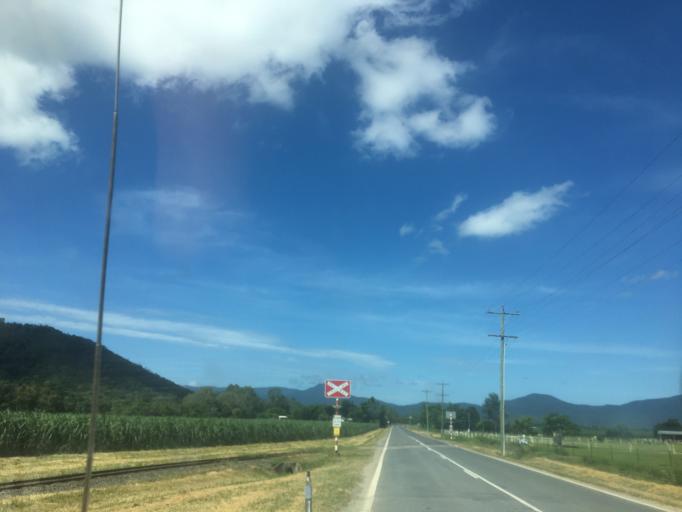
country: AU
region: Queensland
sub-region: Cairns
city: Woree
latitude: -17.0667
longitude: 145.7523
